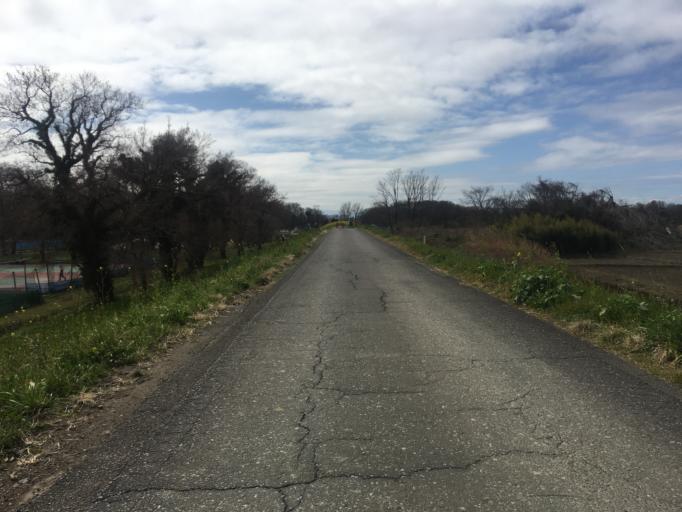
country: JP
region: Saitama
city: Shiki
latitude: 35.8522
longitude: 139.6083
